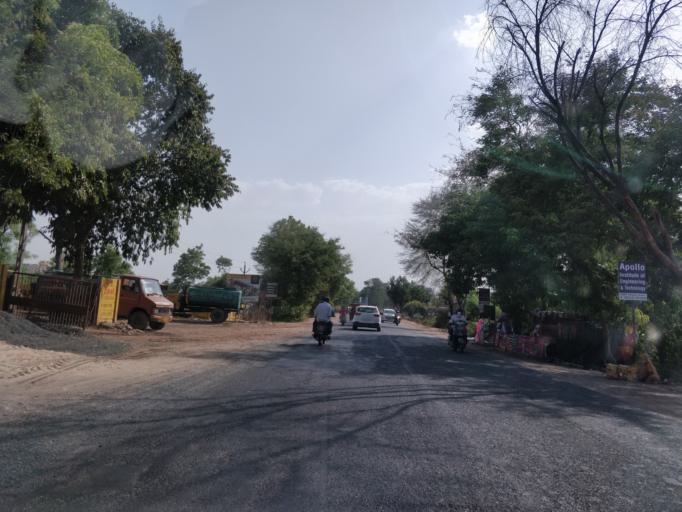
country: IN
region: Gujarat
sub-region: Ahmadabad
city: Naroda
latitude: 23.0902
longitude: 72.6888
